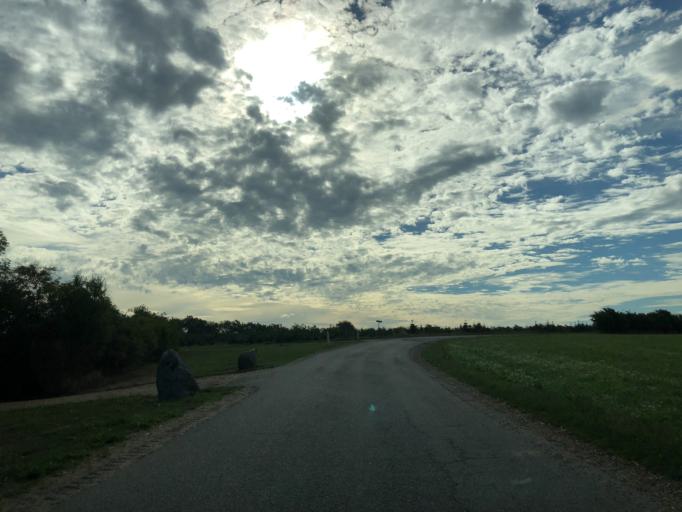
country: DK
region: Central Jutland
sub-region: Holstebro Kommune
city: Ulfborg
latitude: 56.1374
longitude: 8.4058
